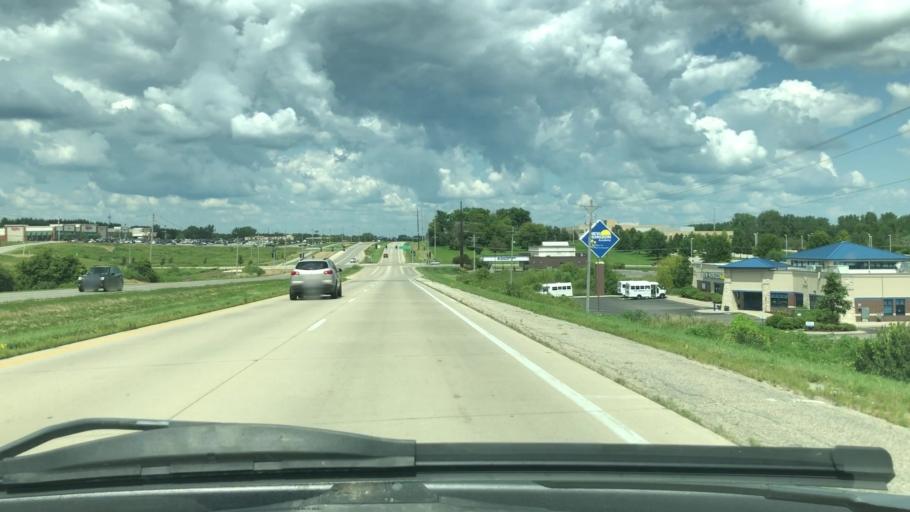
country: US
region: Minnesota
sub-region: Olmsted County
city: Rochester
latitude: 44.0610
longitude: -92.5238
